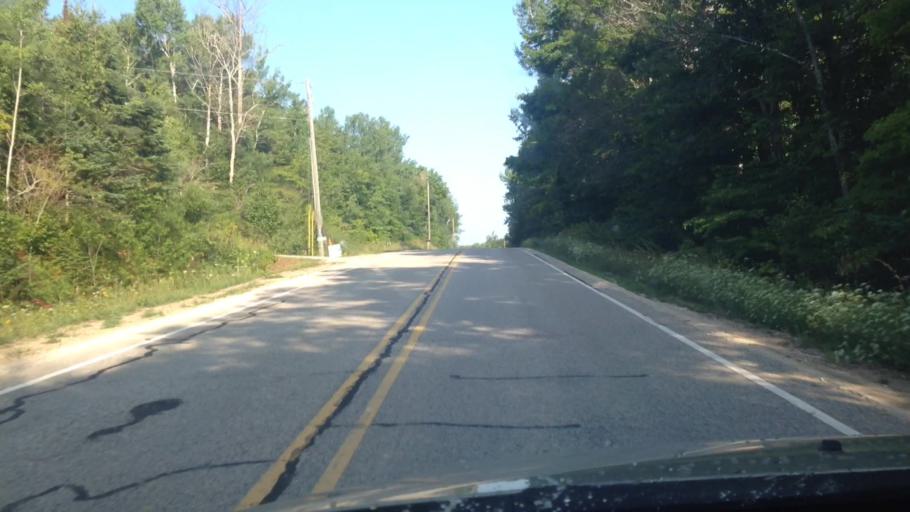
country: US
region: Michigan
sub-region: Mackinac County
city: Saint Ignace
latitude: 45.8918
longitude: -84.7935
